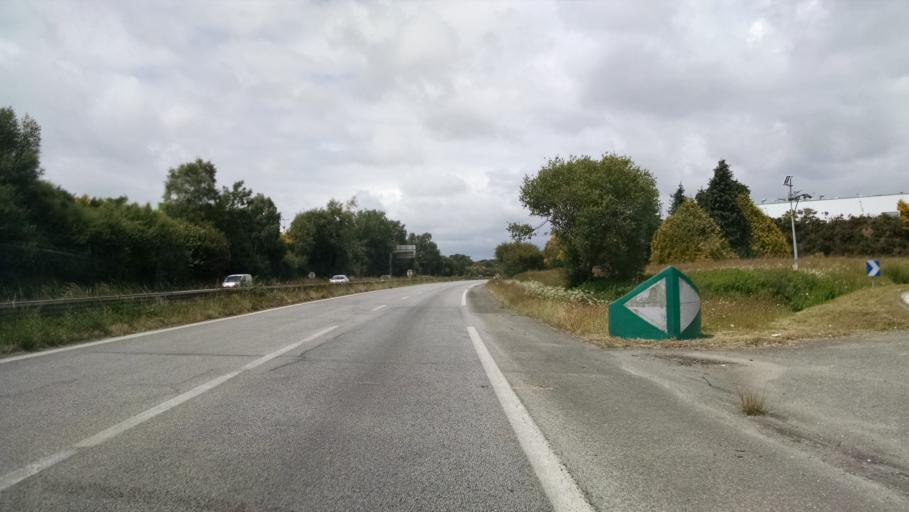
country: FR
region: Brittany
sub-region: Departement du Morbihan
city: Queven
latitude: 47.7792
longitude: -3.4202
